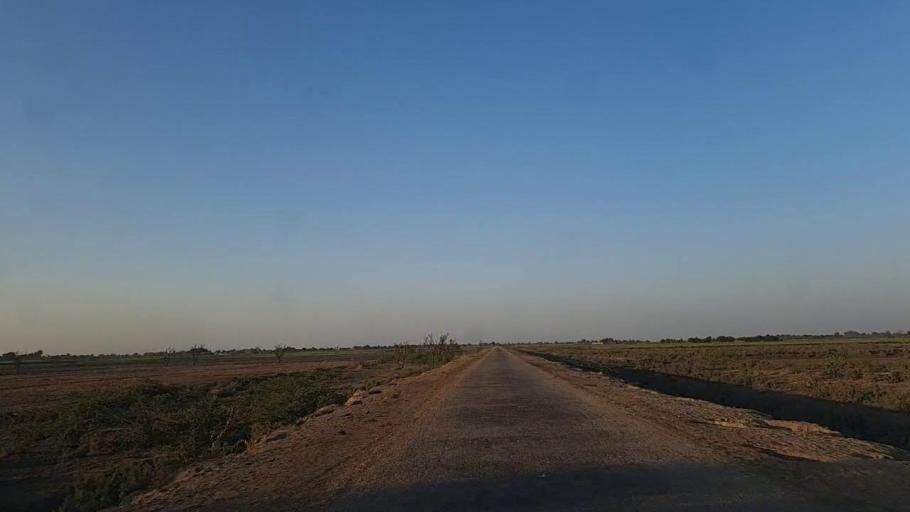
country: PK
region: Sindh
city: Naukot
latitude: 25.0182
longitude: 69.4167
